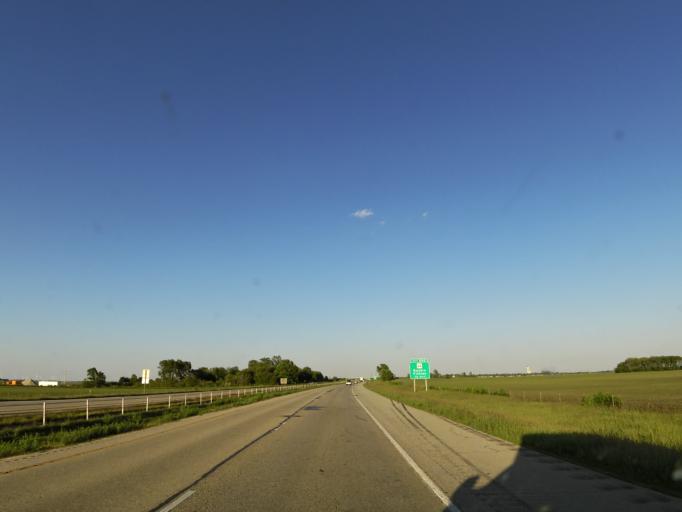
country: US
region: Illinois
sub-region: Champaign County
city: Homer
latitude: 40.1235
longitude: -87.9153
